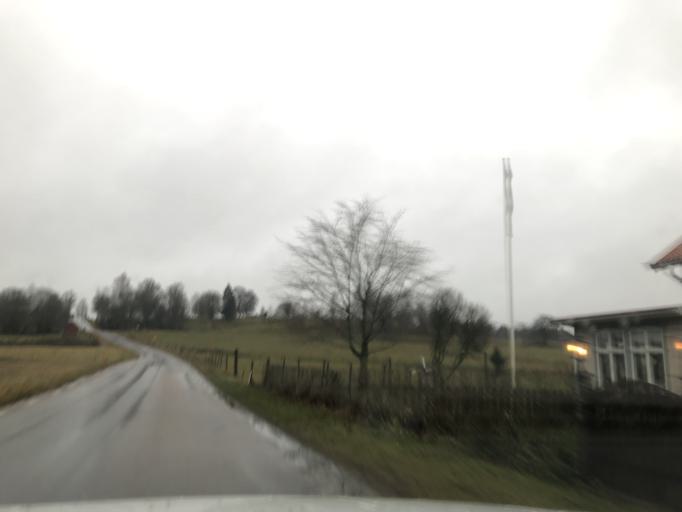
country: SE
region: Vaestra Goetaland
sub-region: Ulricehamns Kommun
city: Ulricehamn
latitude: 57.8510
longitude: 13.5447
